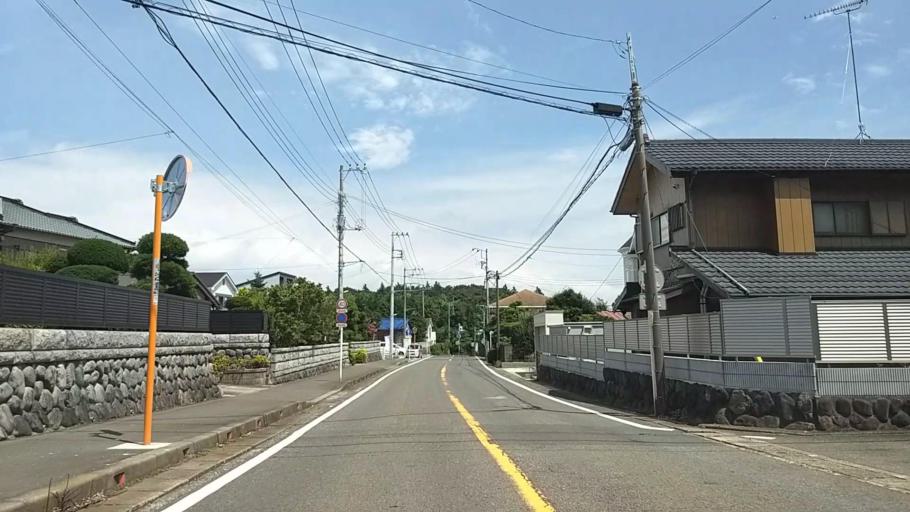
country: JP
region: Kanagawa
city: Fujisawa
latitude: 35.4067
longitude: 139.4336
